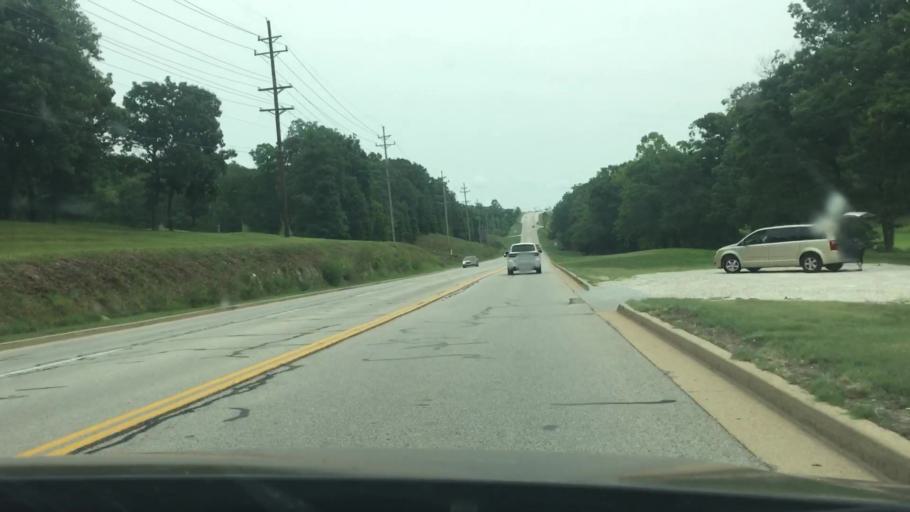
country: US
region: Missouri
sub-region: Miller County
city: Lake Ozark
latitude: 38.1919
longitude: -92.6589
